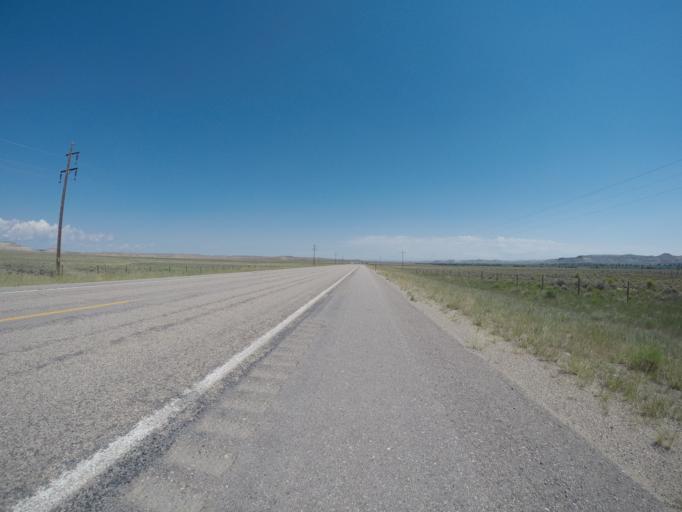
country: US
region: Wyoming
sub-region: Sublette County
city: Marbleton
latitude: 42.4111
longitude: -110.1173
